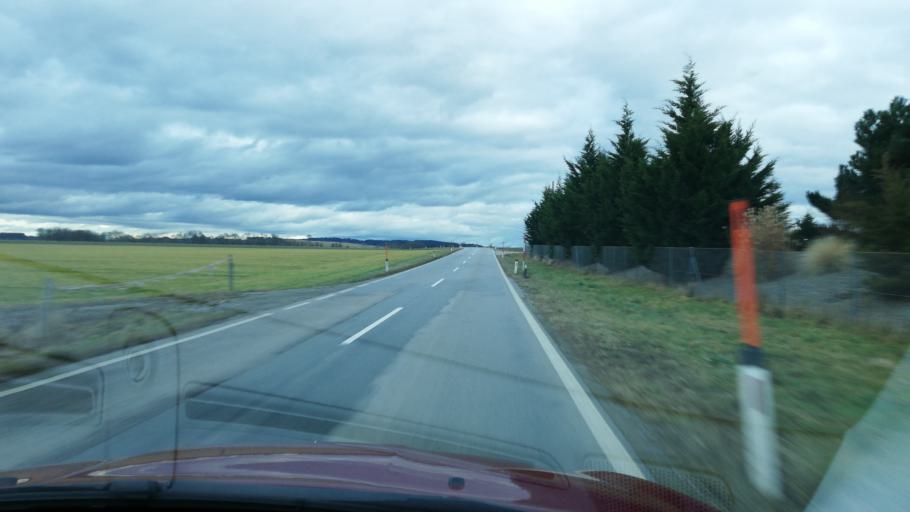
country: DE
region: Bavaria
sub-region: Lower Bavaria
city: Bad Fussing
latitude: 48.2655
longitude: 13.3214
